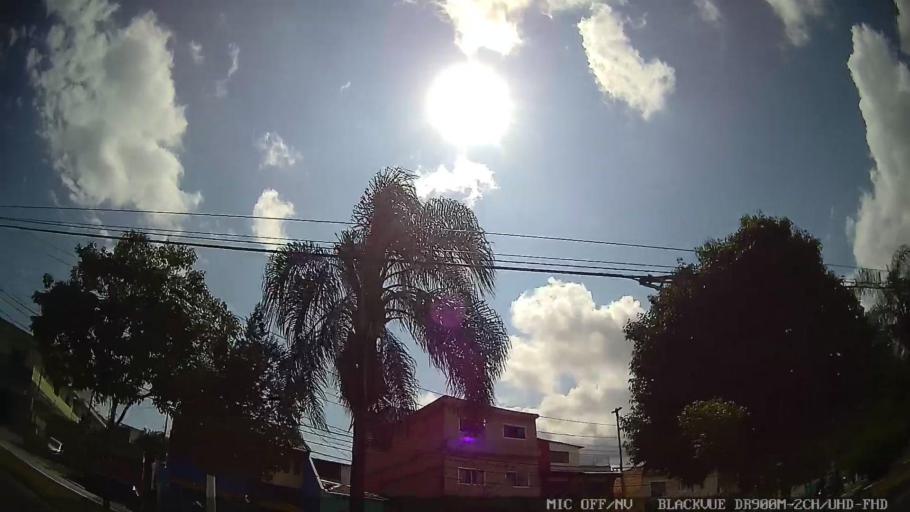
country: BR
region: Sao Paulo
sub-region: Guarulhos
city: Guarulhos
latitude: -23.4933
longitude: -46.4801
